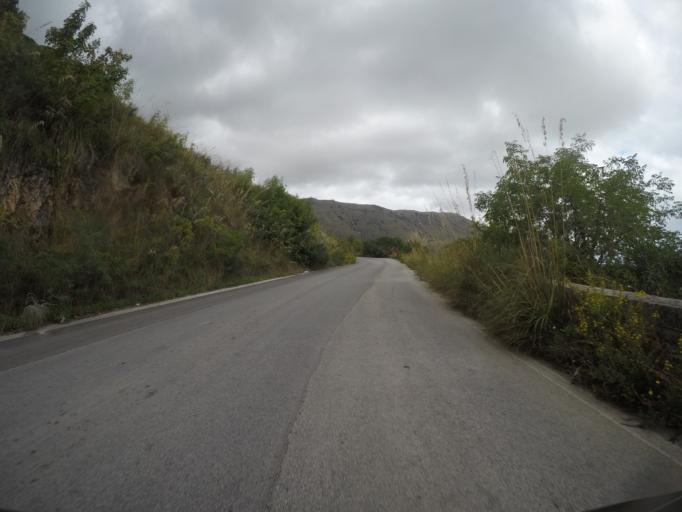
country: IT
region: Sicily
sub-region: Palermo
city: Montelepre
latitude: 38.1191
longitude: 13.1780
